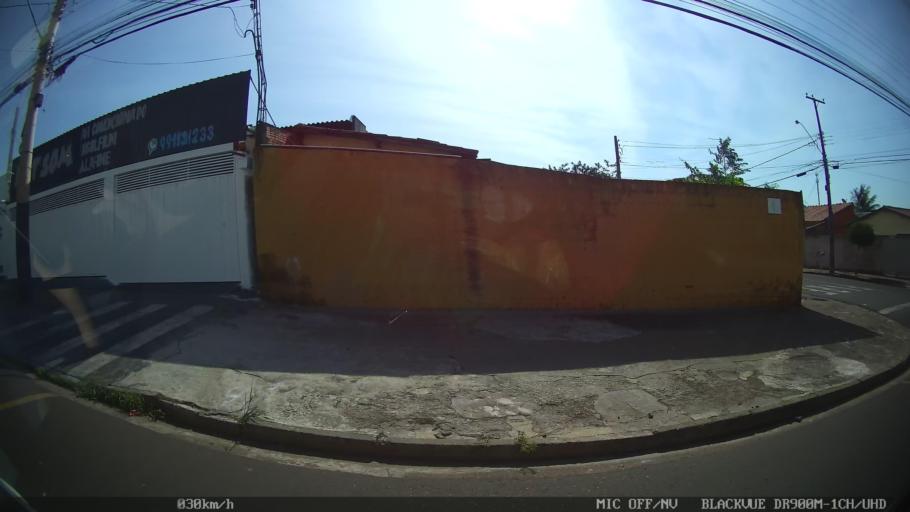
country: BR
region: Sao Paulo
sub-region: Sao Jose Do Rio Preto
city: Sao Jose do Rio Preto
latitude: -20.7936
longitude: -49.4070
